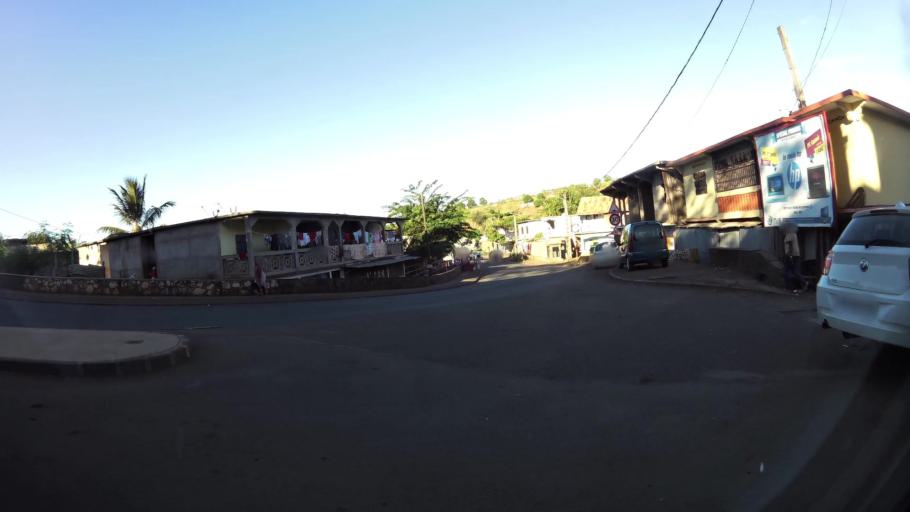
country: YT
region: Koungou
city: Koungou
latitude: -12.7369
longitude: 45.2049
